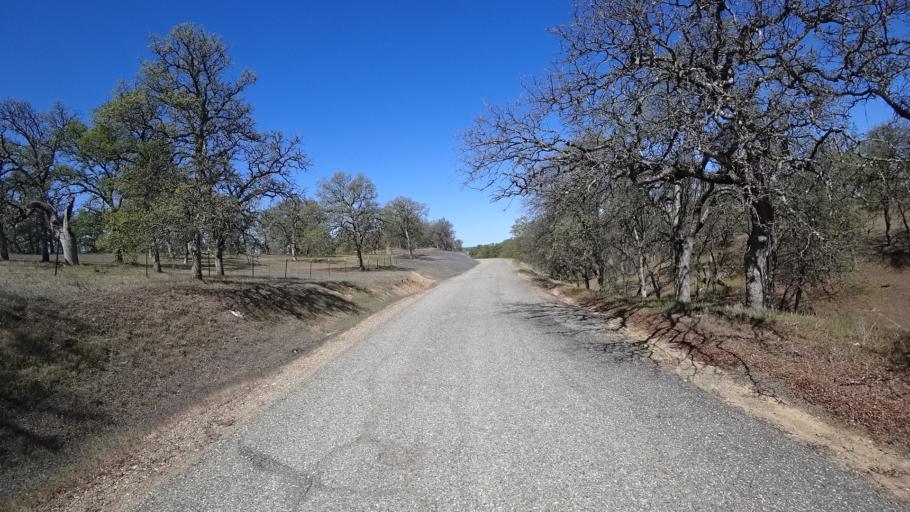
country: US
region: California
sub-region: Glenn County
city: Orland
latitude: 39.7691
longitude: -122.3524
